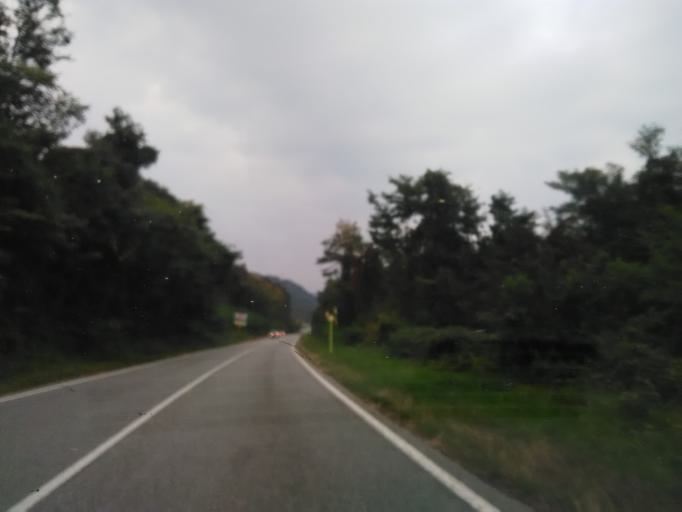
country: IT
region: Piedmont
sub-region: Provincia di Vercelli
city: Borgosesia
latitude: 45.7311
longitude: 8.2603
